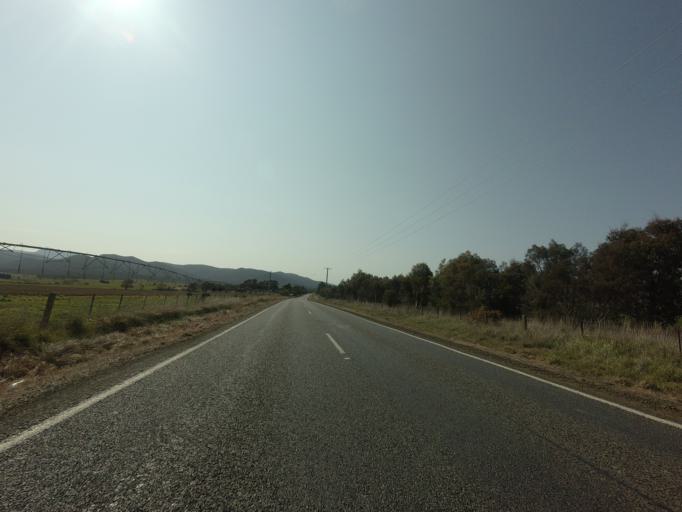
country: AU
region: Tasmania
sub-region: Northern Midlands
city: Evandale
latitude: -41.7903
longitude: 147.7123
